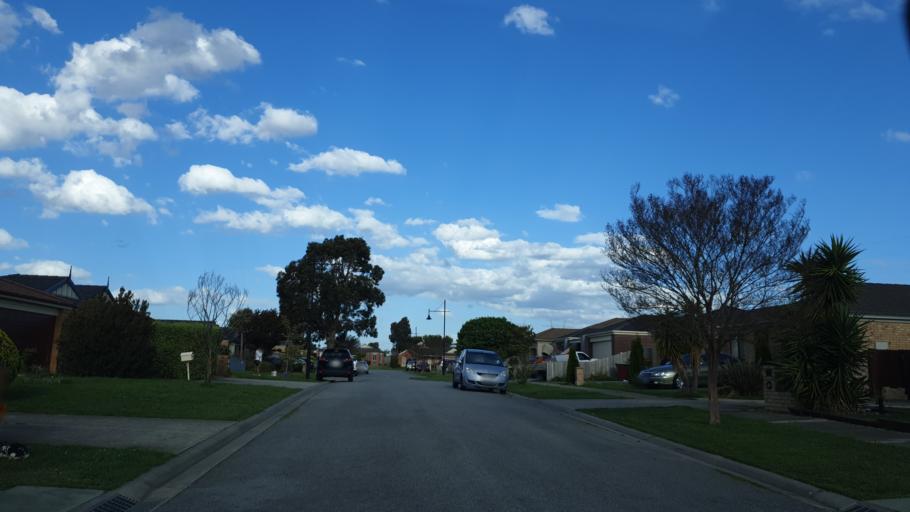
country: AU
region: Victoria
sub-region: Casey
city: Cranbourne North
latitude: -38.0887
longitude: 145.2868
